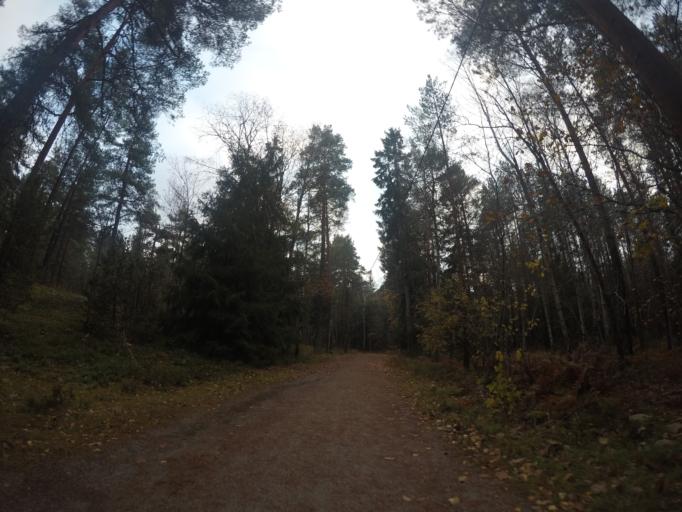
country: SE
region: Soedermanland
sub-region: Eskilstuna Kommun
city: Eskilstuna
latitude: 59.3485
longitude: 16.5228
